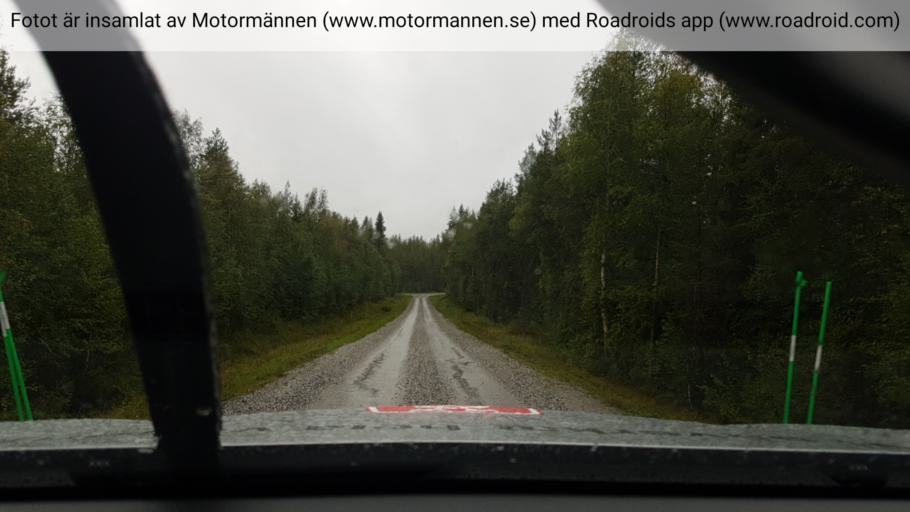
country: SE
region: Vaesterbotten
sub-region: Asele Kommun
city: Asele
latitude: 63.9808
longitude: 17.5859
